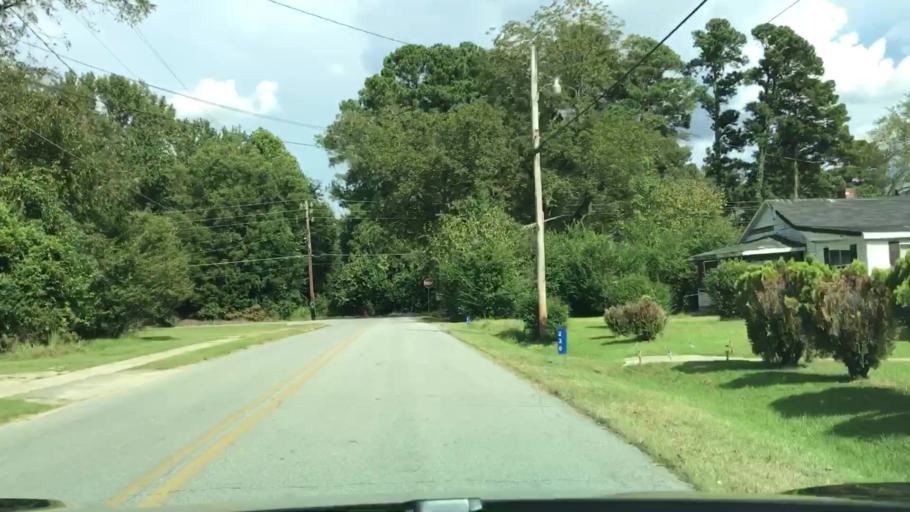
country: US
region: Georgia
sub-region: Jefferson County
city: Wadley
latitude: 32.8630
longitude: -82.3984
